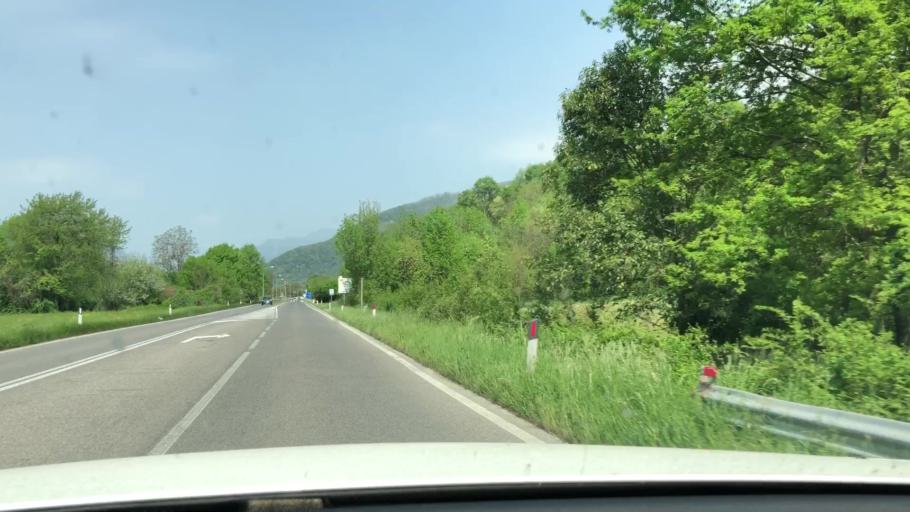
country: IT
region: Friuli Venezia Giulia
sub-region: Provincia di Udine
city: Magnano in Riviera
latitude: 46.2104
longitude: 13.1853
